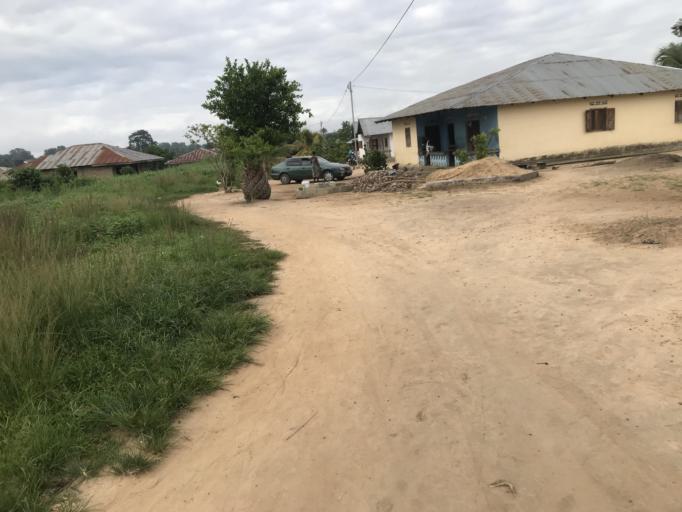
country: SL
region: Eastern Province
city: Pendembu
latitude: 8.0894
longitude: -10.6942
